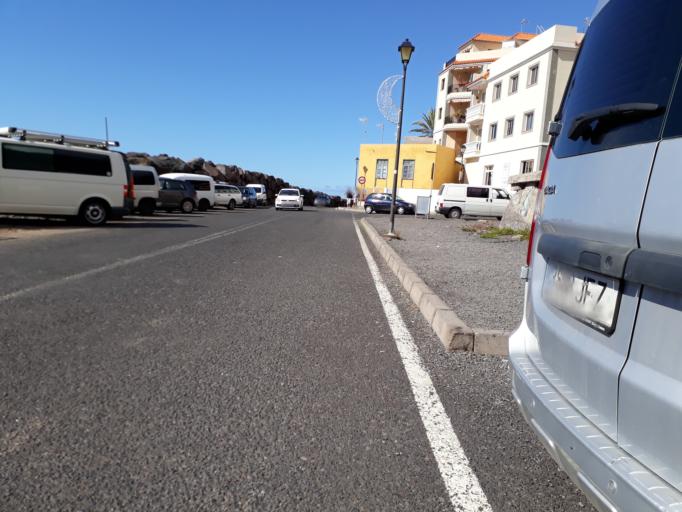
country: ES
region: Canary Islands
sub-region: Provincia de Santa Cruz de Tenerife
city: Alajero
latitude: 28.0826
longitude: -17.3344
